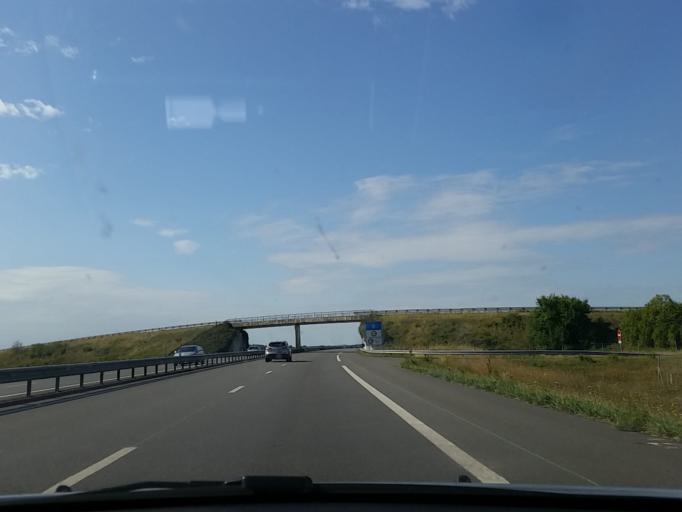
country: FR
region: Centre
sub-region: Departement du Cher
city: Levet
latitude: 46.9633
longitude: 2.4232
